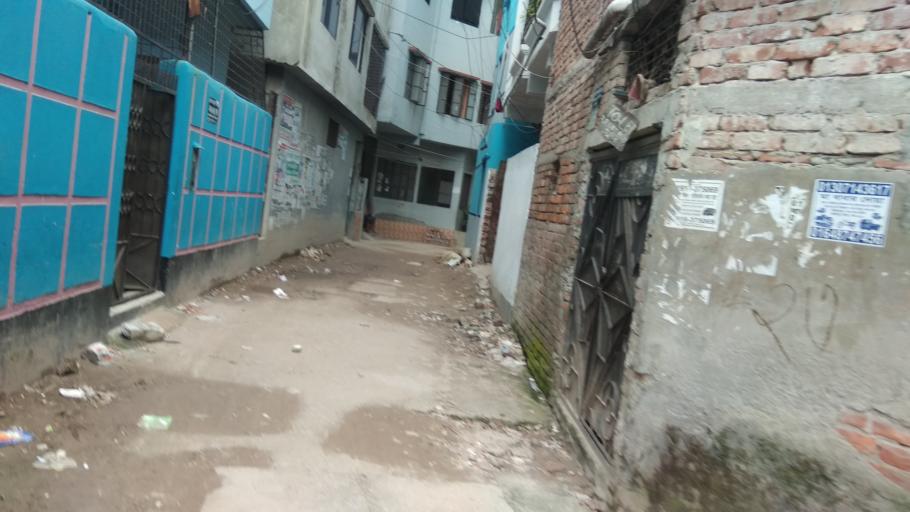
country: BD
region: Dhaka
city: Azimpur
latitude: 23.7991
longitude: 90.3753
